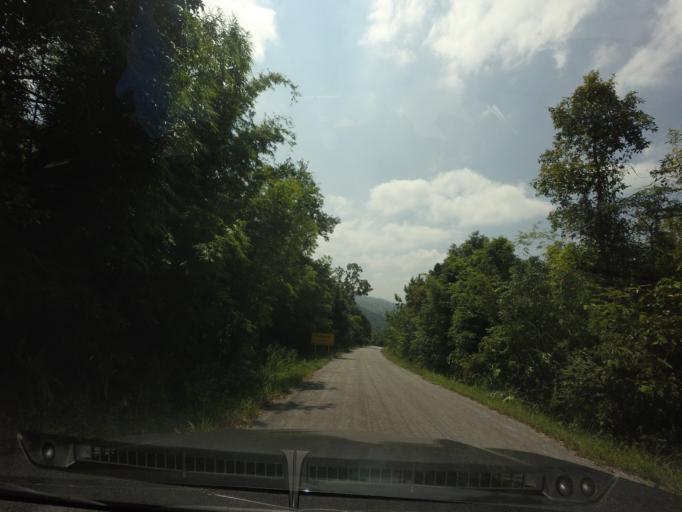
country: TH
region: Loei
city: Na Haeo
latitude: 17.4905
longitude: 100.9390
